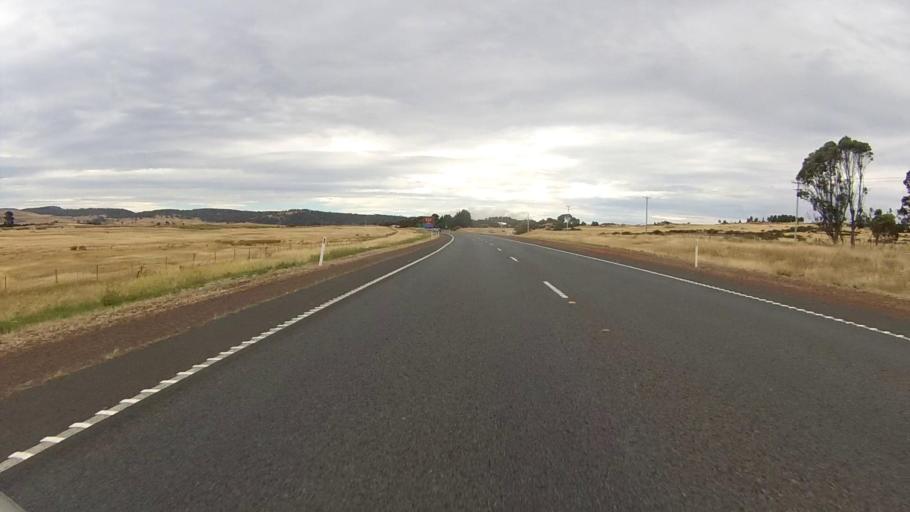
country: AU
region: Tasmania
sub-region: Brighton
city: Bridgewater
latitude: -42.3173
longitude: 147.3524
